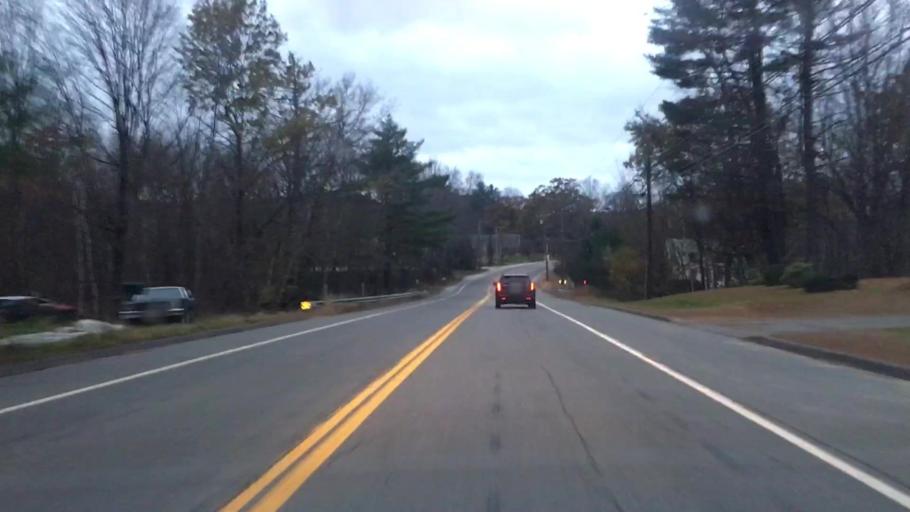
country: US
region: Maine
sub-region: Oxford County
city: Dixfield
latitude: 44.5231
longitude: -70.4504
